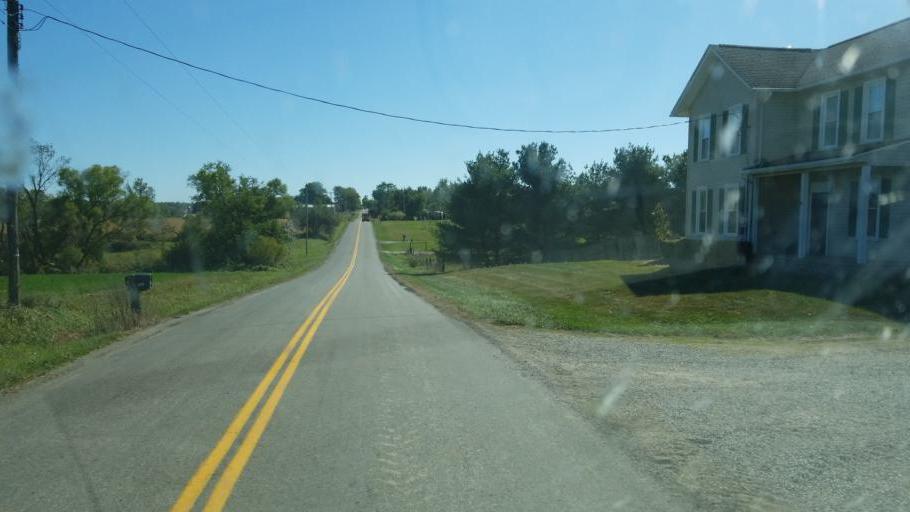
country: US
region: Ohio
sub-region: Wayne County
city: West Salem
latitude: 40.8607
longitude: -82.1745
